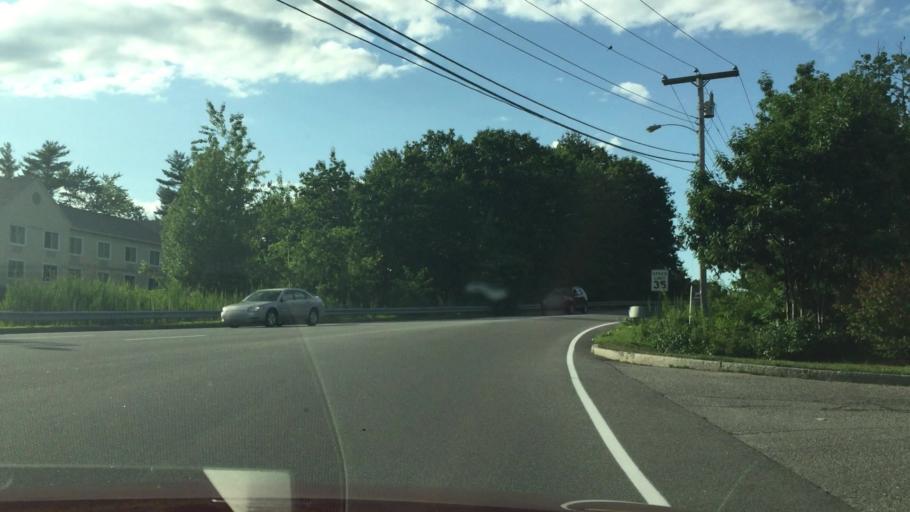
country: US
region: Maine
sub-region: Cumberland County
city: South Portland Gardens
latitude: 43.6267
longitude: -70.3472
